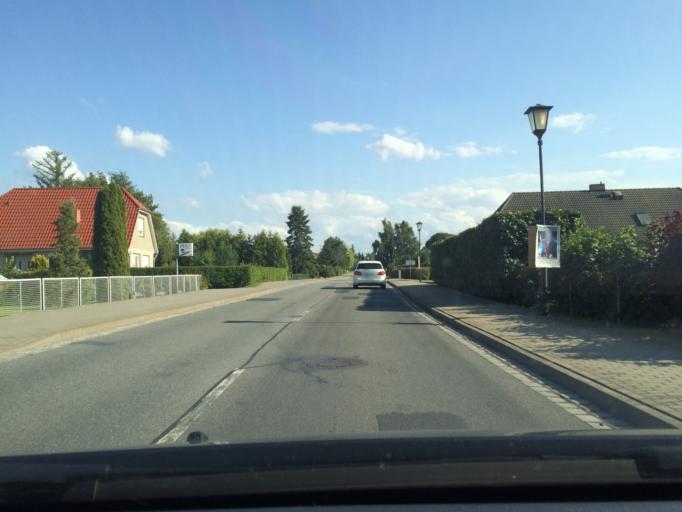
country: DE
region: Mecklenburg-Vorpommern
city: Niepars
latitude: 54.3094
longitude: 12.9250
